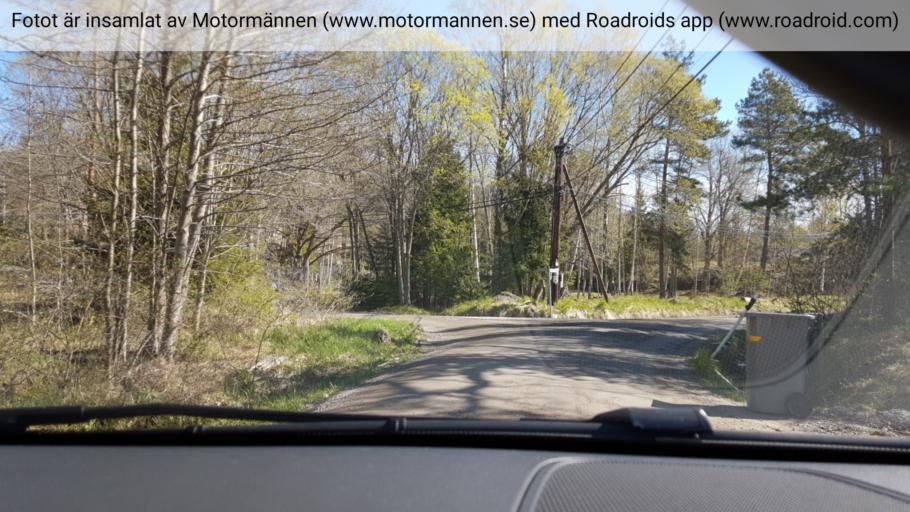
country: SE
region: Stockholm
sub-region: Varmdo Kommun
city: Hemmesta
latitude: 59.2887
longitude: 18.5413
